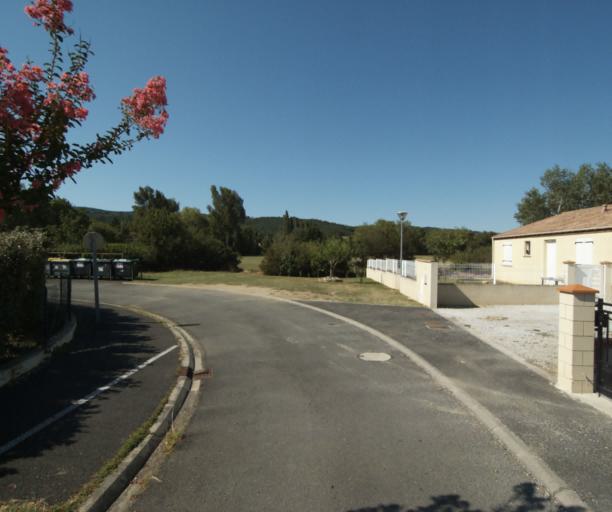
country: FR
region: Midi-Pyrenees
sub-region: Departement du Tarn
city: Soreze
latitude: 43.4540
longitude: 2.0375
